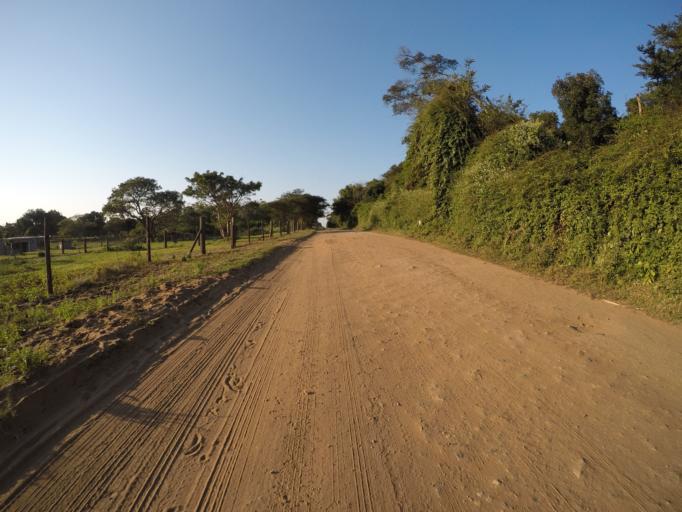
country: ZA
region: KwaZulu-Natal
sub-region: uThungulu District Municipality
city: KwaMbonambi
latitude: -28.7041
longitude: 32.1887
